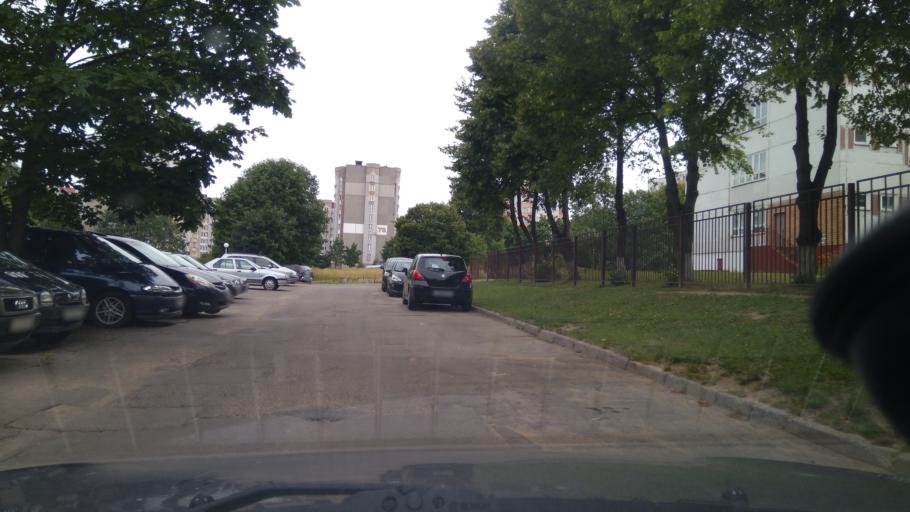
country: BY
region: Minsk
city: Novoye Medvezhino
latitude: 53.8947
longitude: 27.4466
